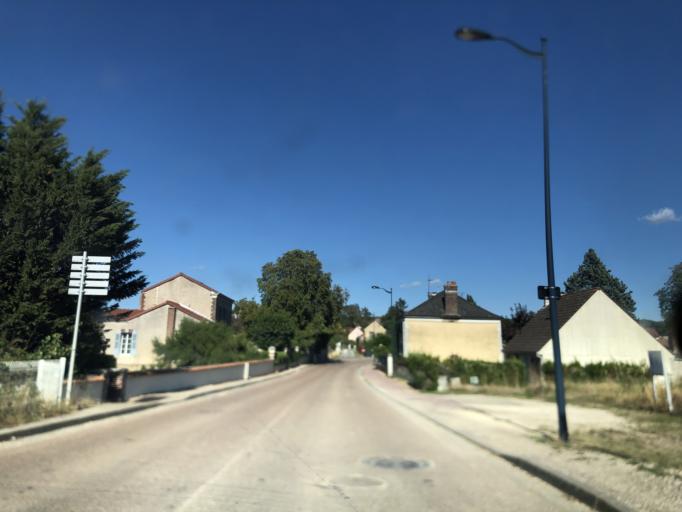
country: FR
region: Bourgogne
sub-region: Departement de l'Yonne
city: Gurgy
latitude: 47.8982
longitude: 3.5536
